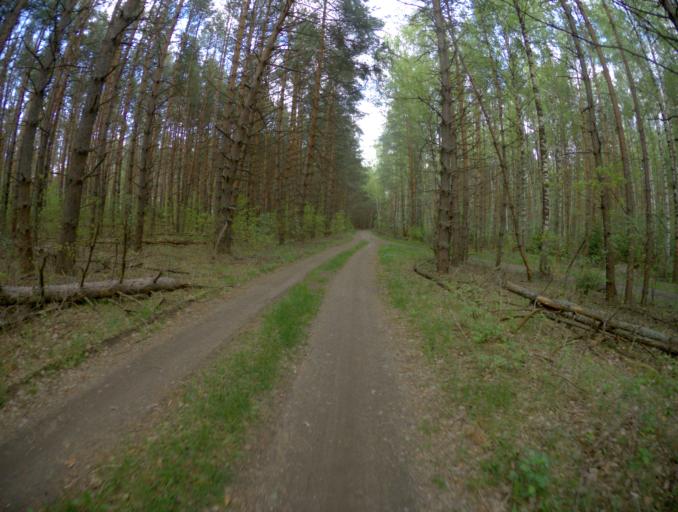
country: RU
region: Rjazan
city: Spas-Klepiki
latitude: 55.2532
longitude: 40.1025
